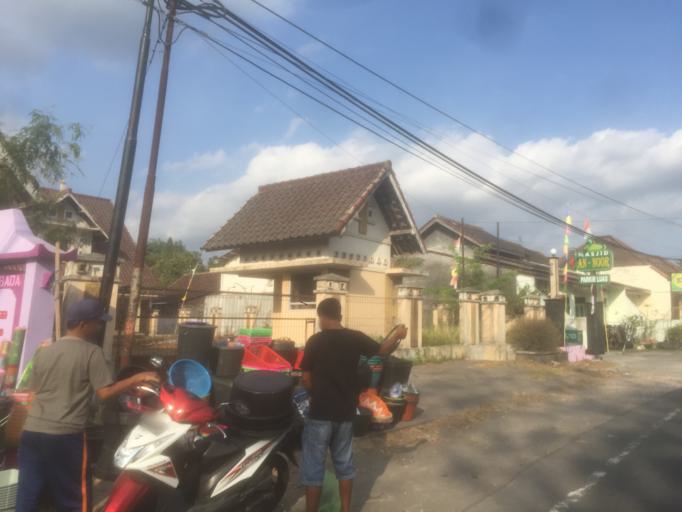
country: ID
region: Daerah Istimewa Yogyakarta
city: Melati
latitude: -7.7197
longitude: 110.3761
